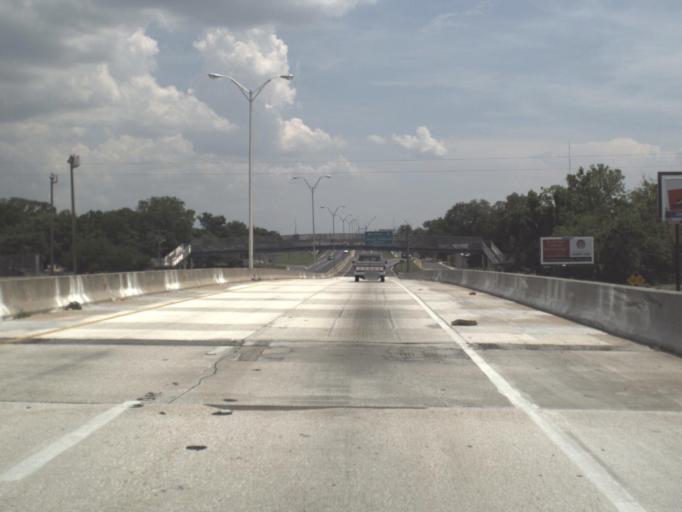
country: US
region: Florida
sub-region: Duval County
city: Jacksonville
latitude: 30.3496
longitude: -81.6369
